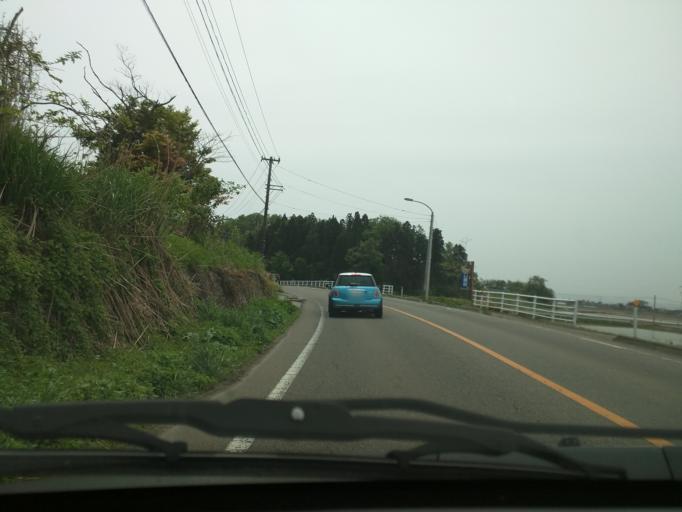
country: JP
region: Niigata
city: Mitsuke
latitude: 37.5622
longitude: 138.9329
